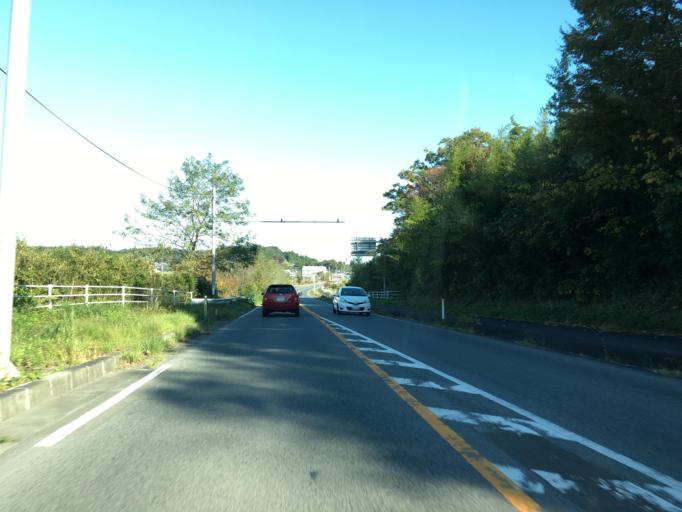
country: JP
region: Miyagi
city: Marumori
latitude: 37.8456
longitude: 140.9168
